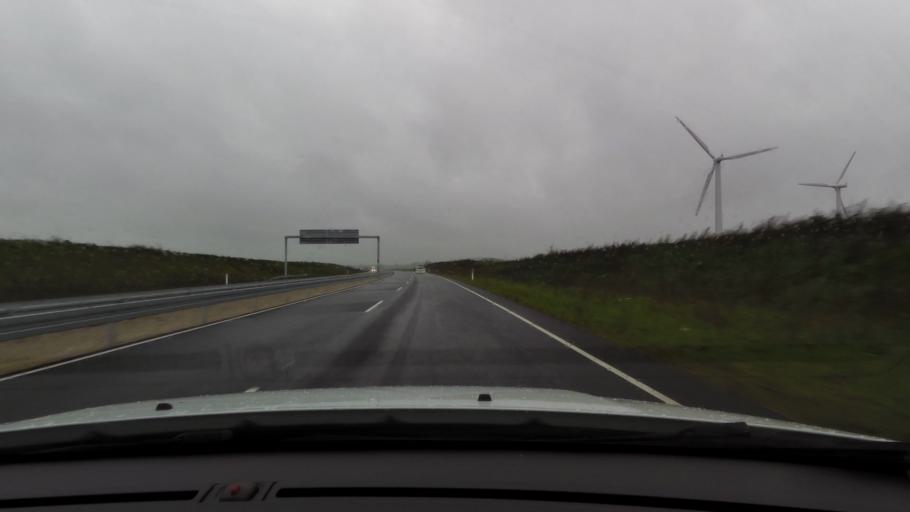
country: DK
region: Capital Region
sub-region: Frederikssund Kommune
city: Skibby
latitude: 55.8000
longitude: 11.9912
